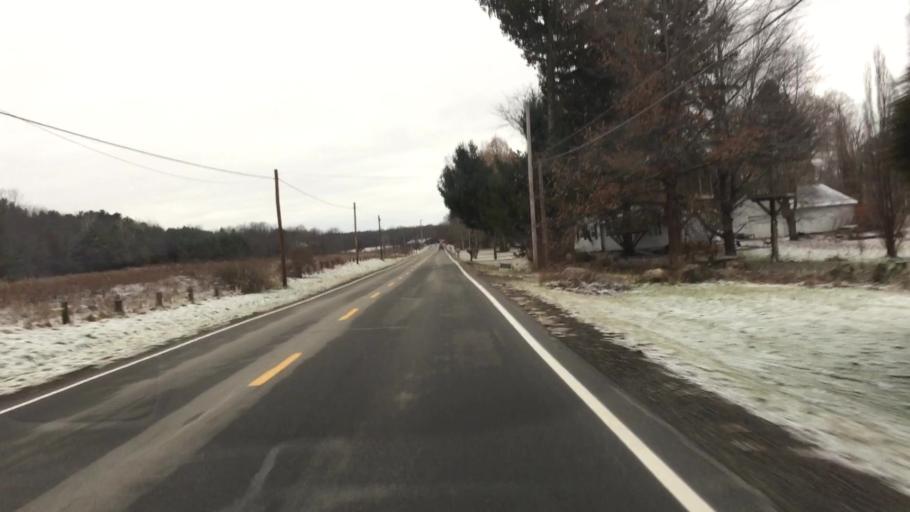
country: US
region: Ohio
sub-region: Summit County
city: Norton
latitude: 41.0717
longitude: -81.6309
